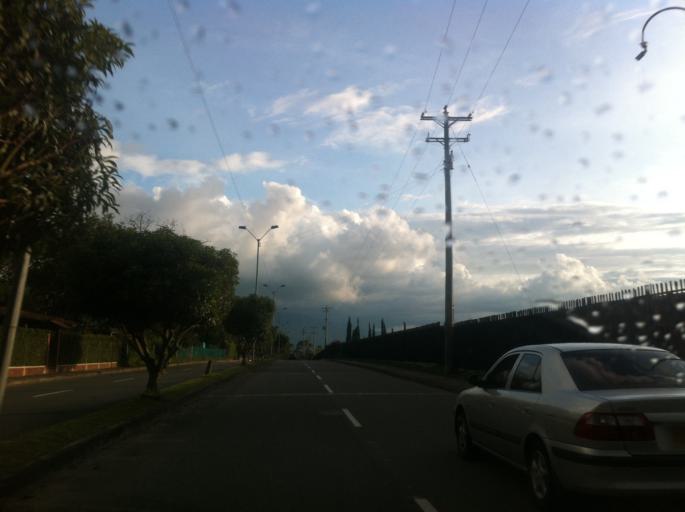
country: CO
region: Quindio
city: Circasia
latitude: 4.5798
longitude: -75.6374
